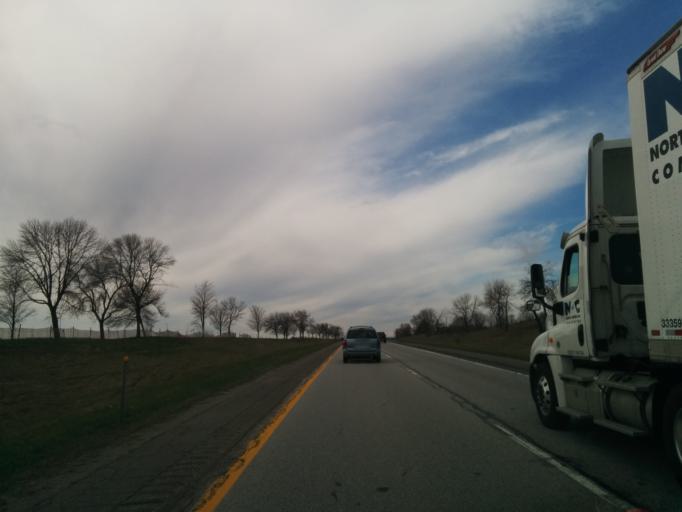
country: US
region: Michigan
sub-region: Ottawa County
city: Hudsonville
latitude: 42.8262
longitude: -85.9255
